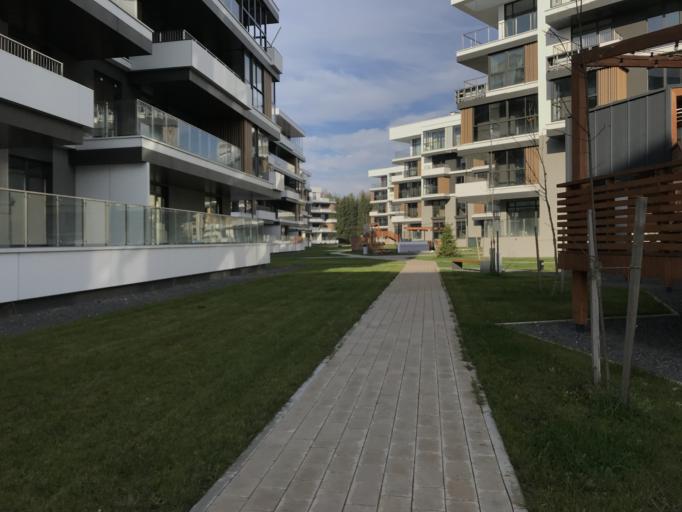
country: BY
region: Minsk
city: Khatsyezhyna
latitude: 53.9463
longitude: 27.3320
